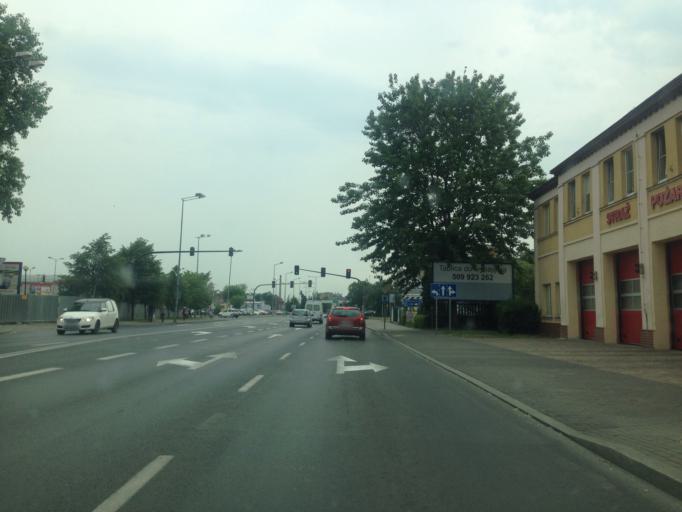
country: PL
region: Kujawsko-Pomorskie
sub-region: Grudziadz
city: Grudziadz
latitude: 53.4906
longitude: 18.7580
